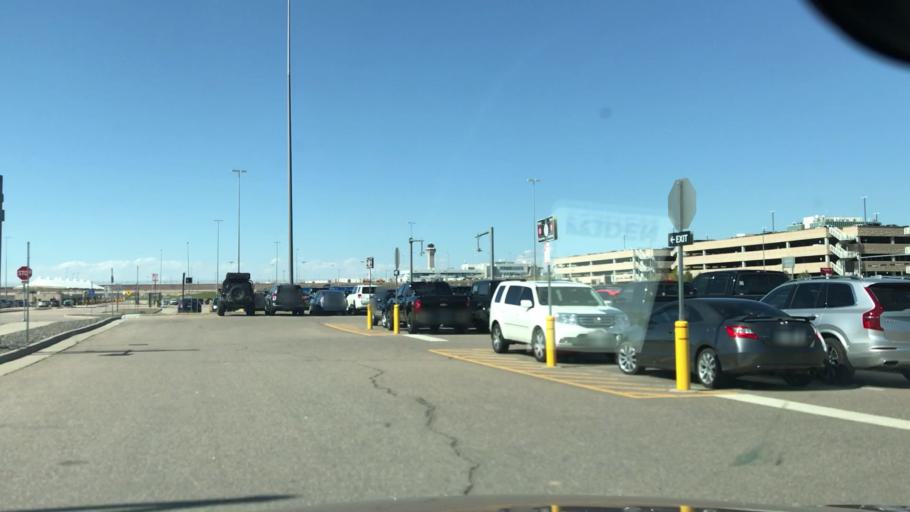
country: US
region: Colorado
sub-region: Weld County
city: Lochbuie
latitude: 39.8476
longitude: -104.6791
